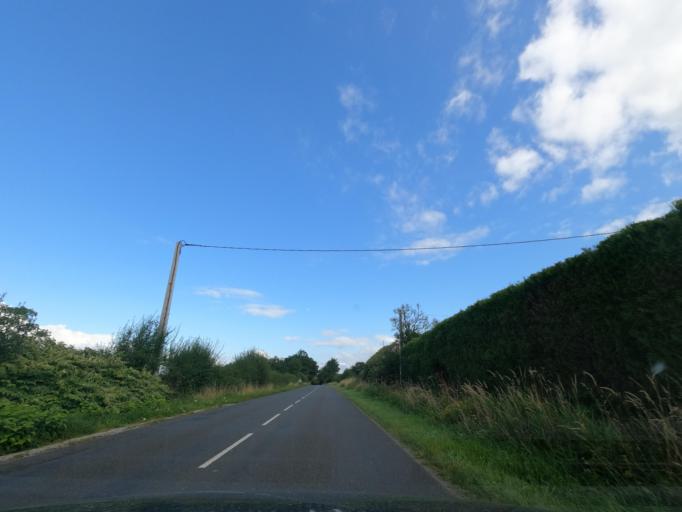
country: FR
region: Lower Normandy
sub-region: Departement de l'Orne
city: Gace
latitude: 48.7562
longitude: 0.2068
